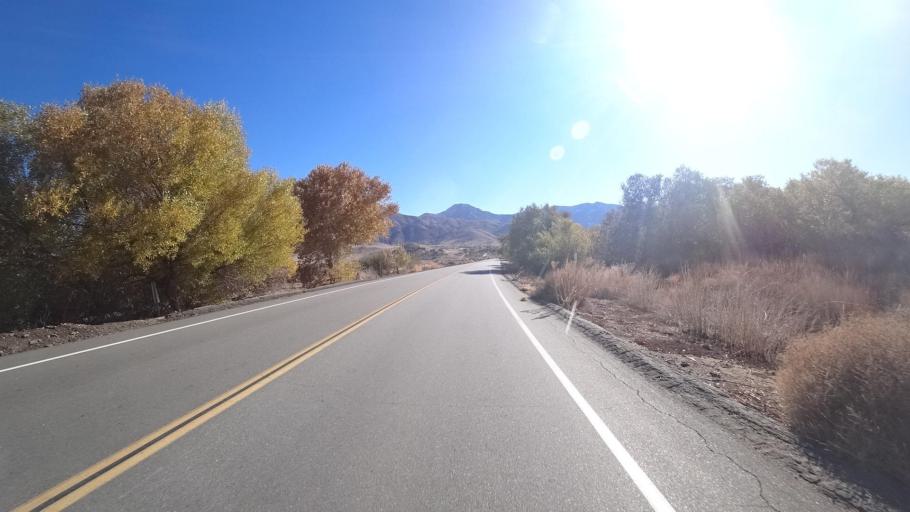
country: US
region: California
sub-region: Kern County
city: Weldon
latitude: 35.6683
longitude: -118.3228
